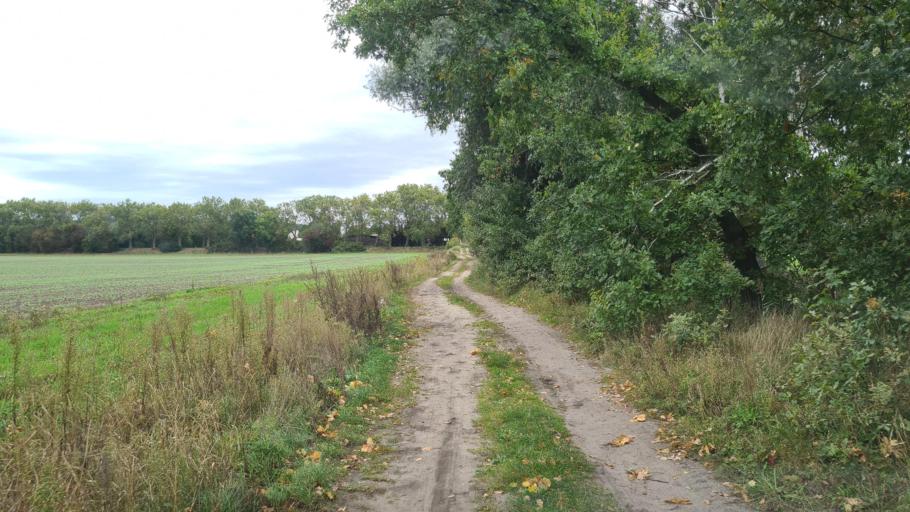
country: DE
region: Brandenburg
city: Zossen
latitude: 52.2465
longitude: 13.4853
